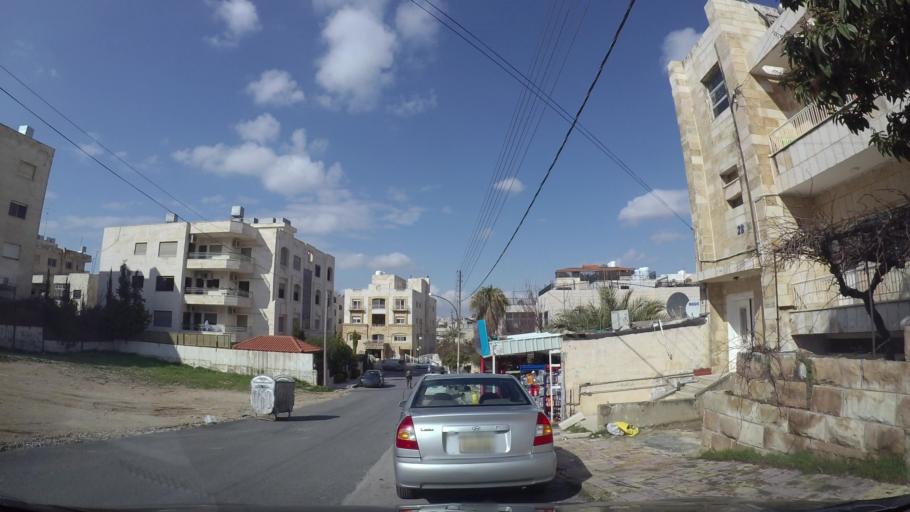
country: JO
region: Amman
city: Al Jubayhah
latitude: 31.9752
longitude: 35.8913
